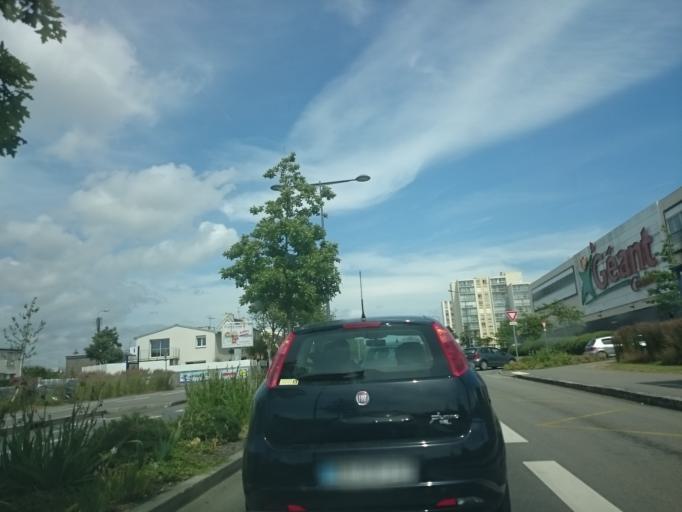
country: FR
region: Brittany
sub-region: Departement du Finistere
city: Brest
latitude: 48.4089
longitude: -4.4672
